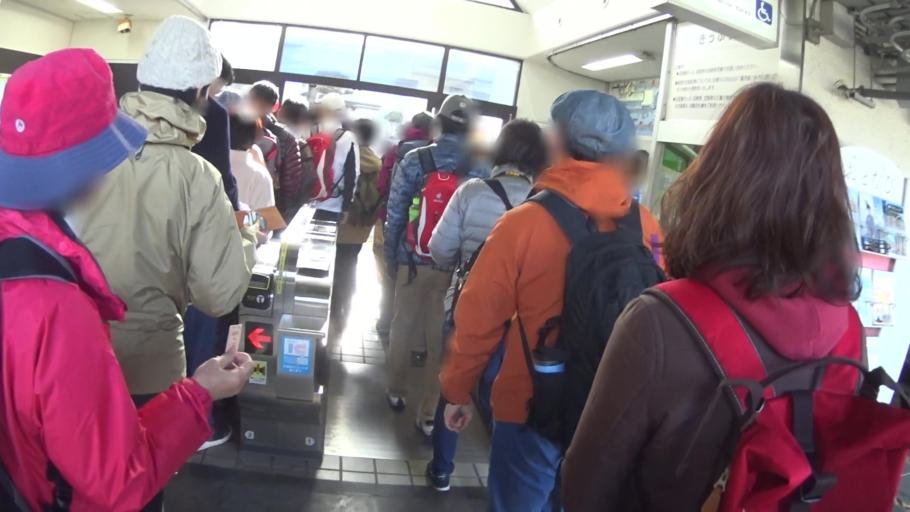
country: JP
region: Hyogo
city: Takarazuka
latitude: 34.8188
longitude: 135.3239
